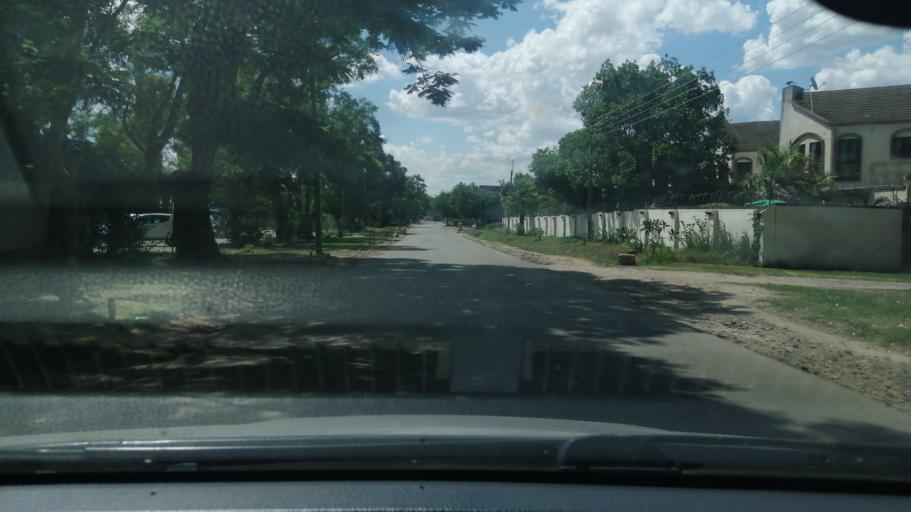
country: ZW
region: Harare
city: Harare
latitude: -17.8114
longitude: 31.0767
